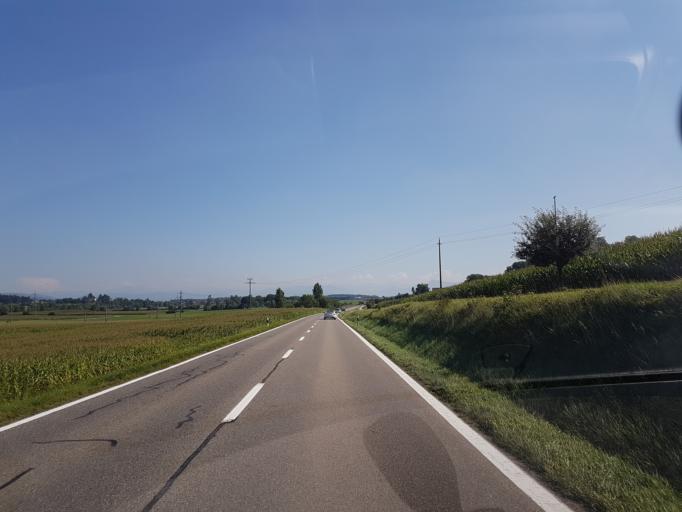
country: CH
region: Aargau
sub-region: Bezirk Muri
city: Waltenschwil
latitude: 47.3212
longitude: 8.3001
